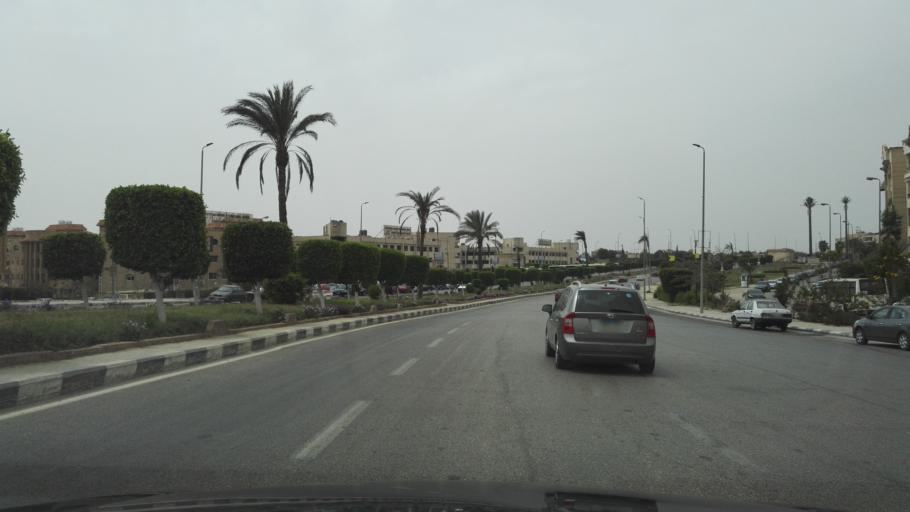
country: EG
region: Muhafazat al Qahirah
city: Cairo
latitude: 29.9909
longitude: 31.4221
